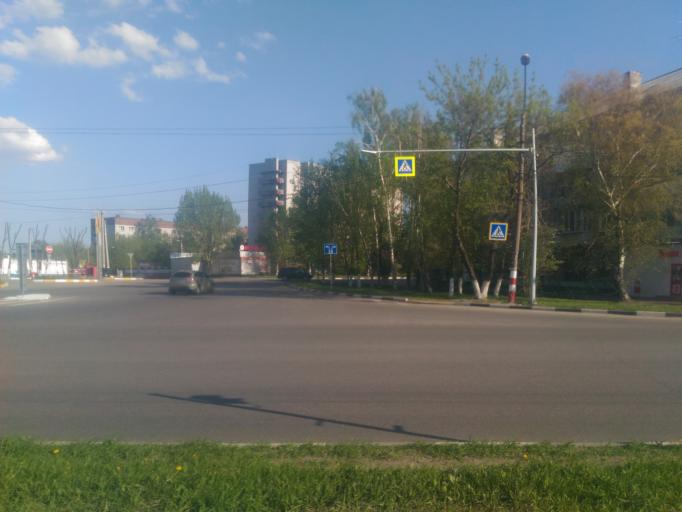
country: RU
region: Ulyanovsk
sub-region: Ulyanovskiy Rayon
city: Ulyanovsk
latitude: 54.2788
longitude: 48.3430
